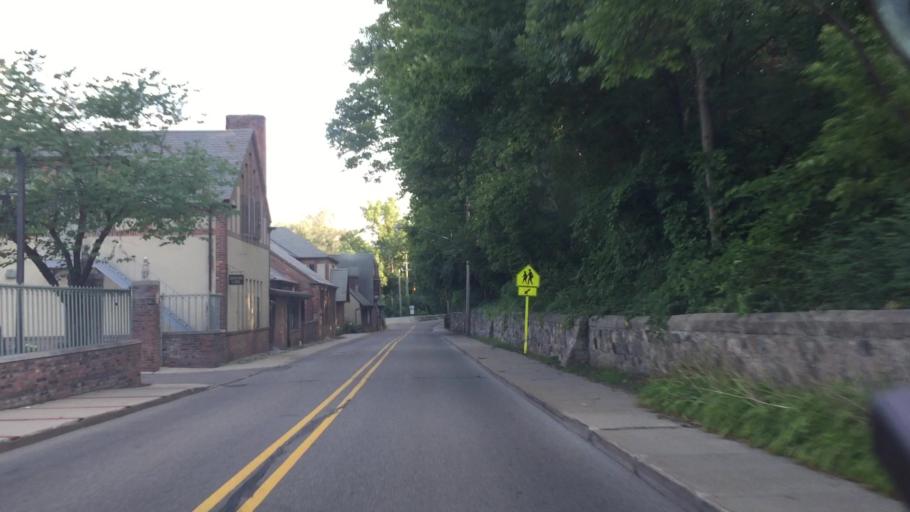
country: US
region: Michigan
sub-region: Oakland County
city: Bloomfield Hills
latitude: 42.5688
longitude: -83.2432
